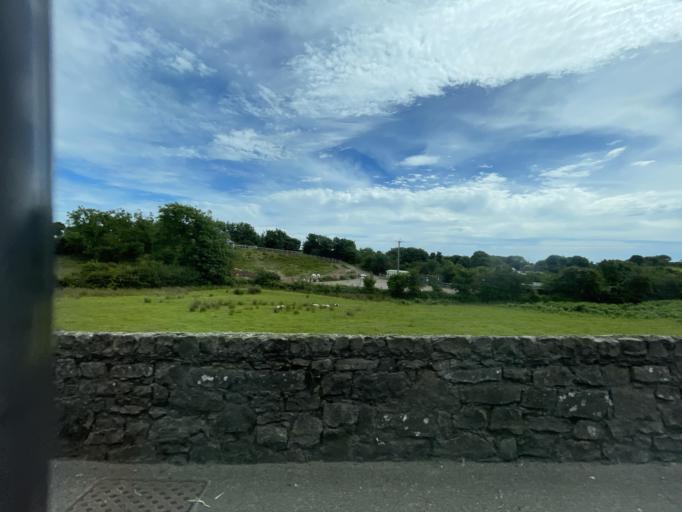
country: GB
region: Wales
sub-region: Anglesey
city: Llangefni
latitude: 53.2588
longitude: -4.4212
